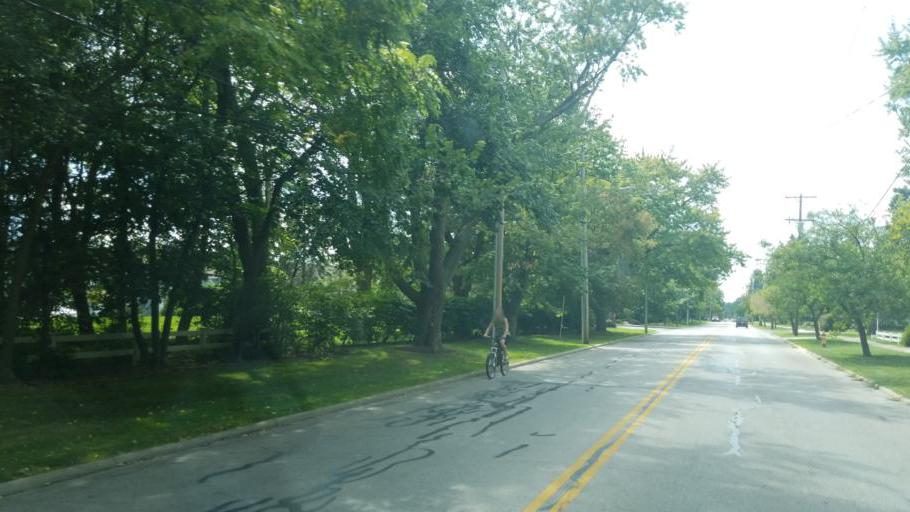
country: US
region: Ohio
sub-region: Wood County
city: Perrysburg
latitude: 41.5735
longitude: -83.6283
